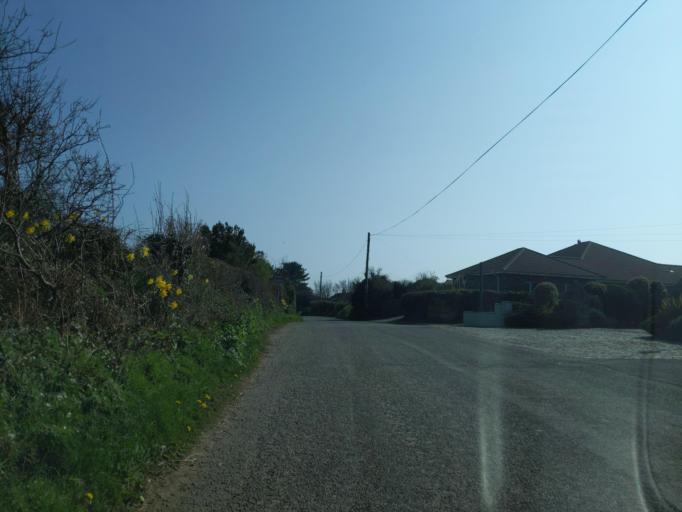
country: GB
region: England
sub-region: Devon
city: Dartmouth
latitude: 50.3133
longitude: -3.6323
